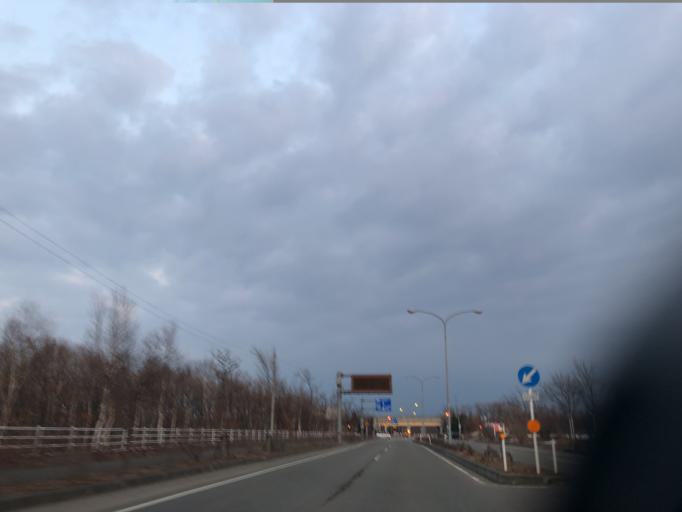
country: JP
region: Hokkaido
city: Chitose
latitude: 42.8192
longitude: 141.6788
